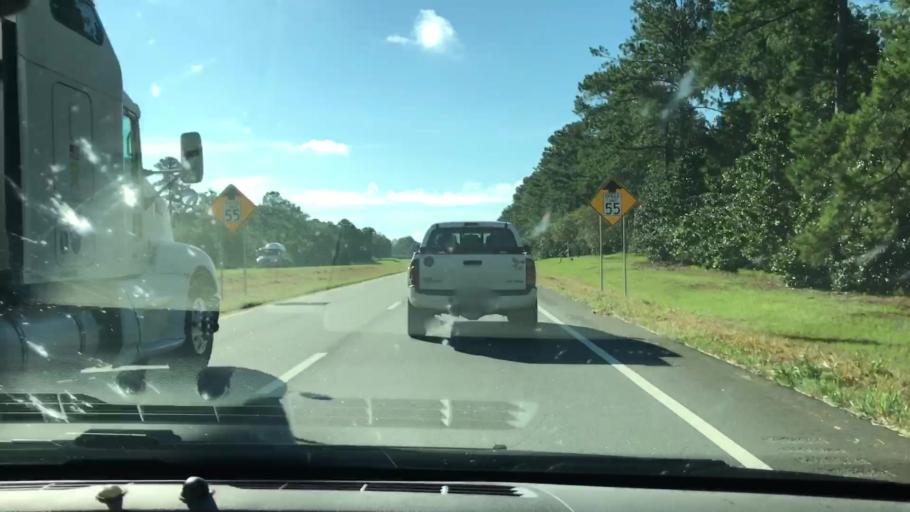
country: US
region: Georgia
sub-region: Lee County
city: Leesburg
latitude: 31.6504
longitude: -84.2640
